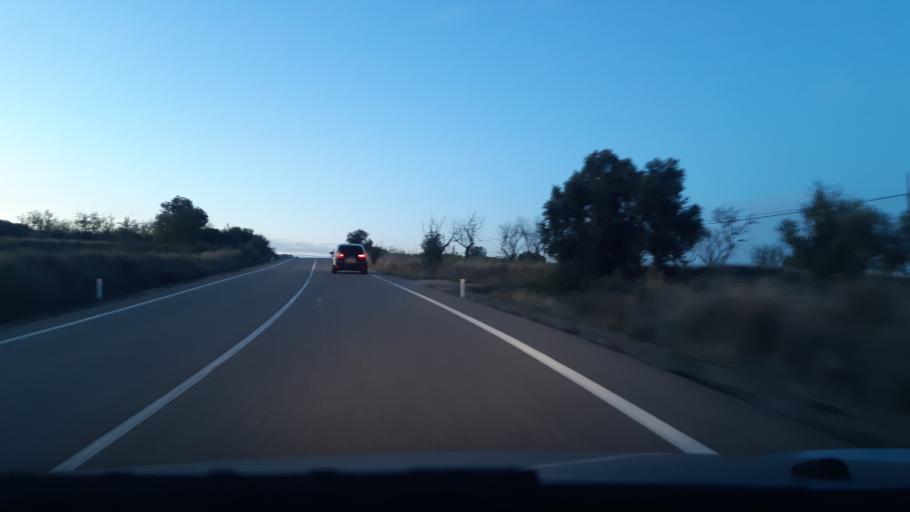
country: ES
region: Aragon
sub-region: Provincia de Teruel
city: Calaceite
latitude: 40.9902
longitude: 0.1990
